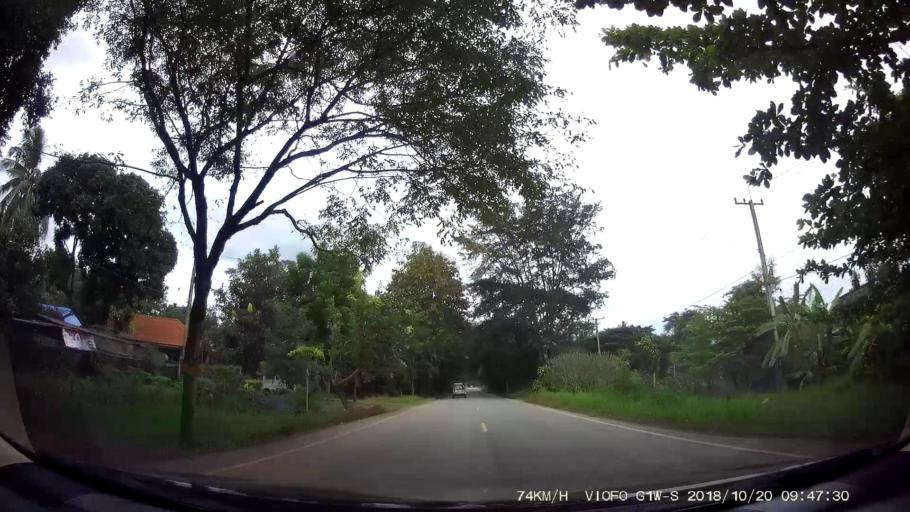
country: TH
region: Chaiyaphum
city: Khon San
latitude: 16.5042
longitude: 101.9190
